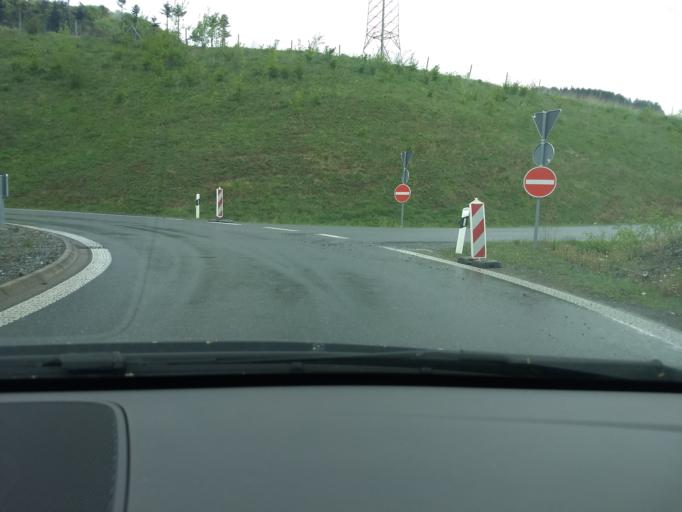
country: DE
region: North Rhine-Westphalia
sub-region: Regierungsbezirk Arnsberg
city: Bestwig
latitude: 51.3617
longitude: 8.3659
